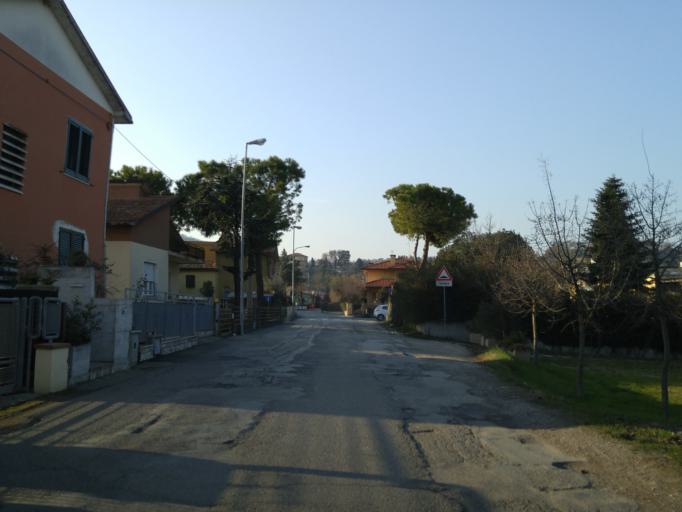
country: IT
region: The Marches
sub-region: Provincia di Pesaro e Urbino
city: Rosciano
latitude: 43.8180
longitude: 12.9953
